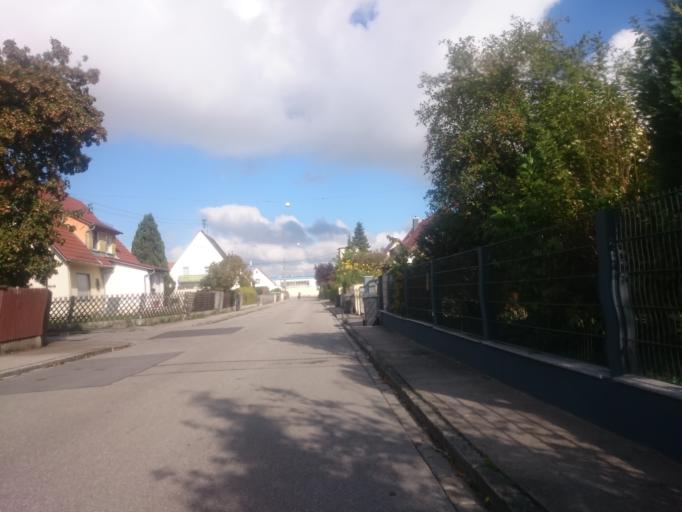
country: DE
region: Bavaria
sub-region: Swabia
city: Friedberg
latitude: 48.3780
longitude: 10.9456
